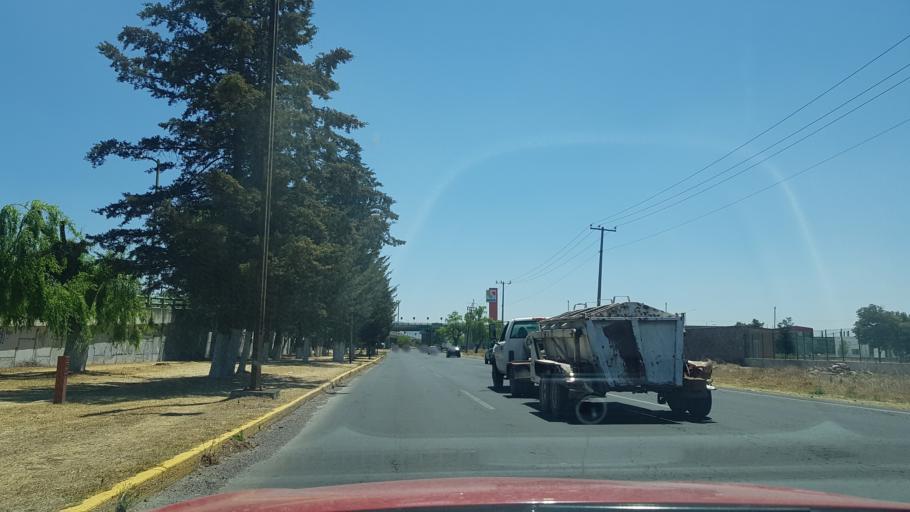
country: MX
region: Mexico
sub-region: Atlacomulco
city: Santa Cruz Bombatevi
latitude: 19.7943
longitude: -99.8895
